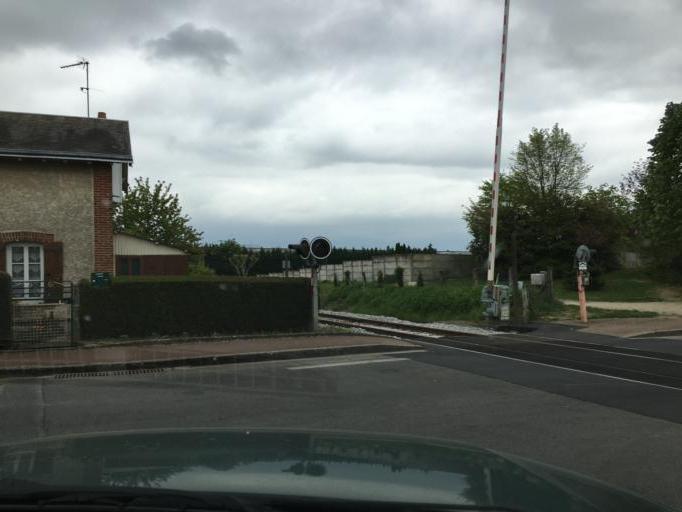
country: FR
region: Centre
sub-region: Departement du Loiret
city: Saint-Jean-de-la-Ruelle
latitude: 47.9180
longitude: 1.8751
